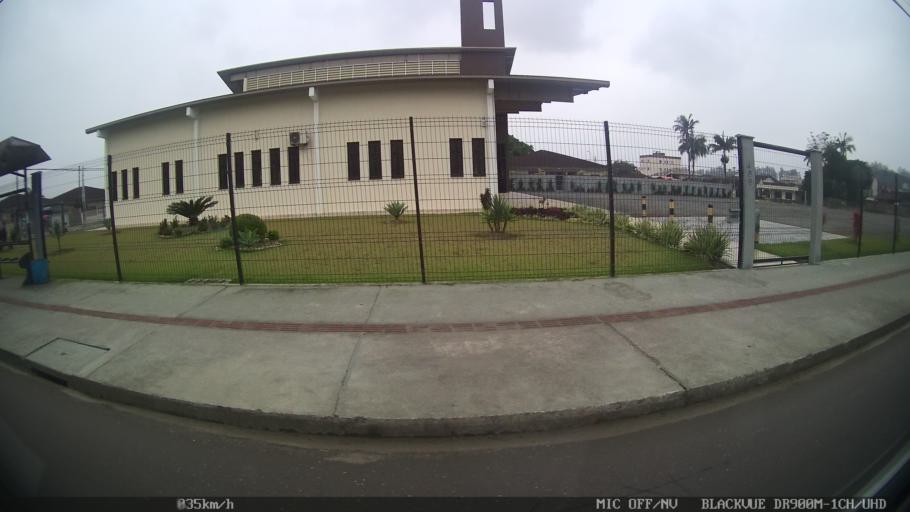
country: BR
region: Santa Catarina
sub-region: Joinville
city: Joinville
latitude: -26.2765
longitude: -48.8073
